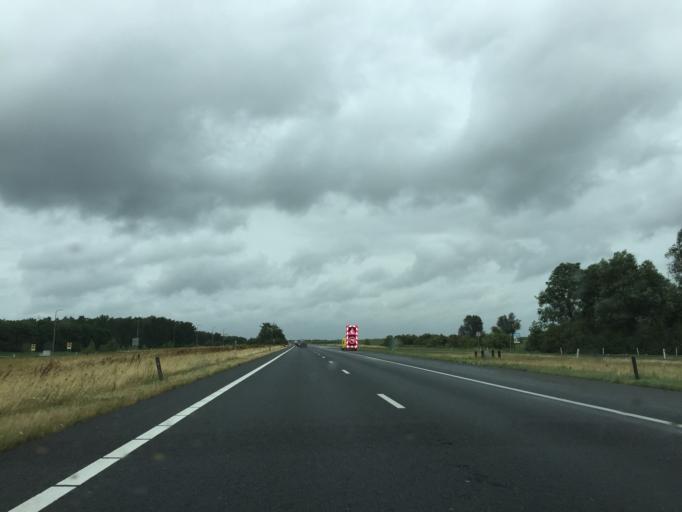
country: NL
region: Flevoland
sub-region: Gemeente Lelystad
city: Lelystad
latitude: 52.4351
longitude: 5.4255
